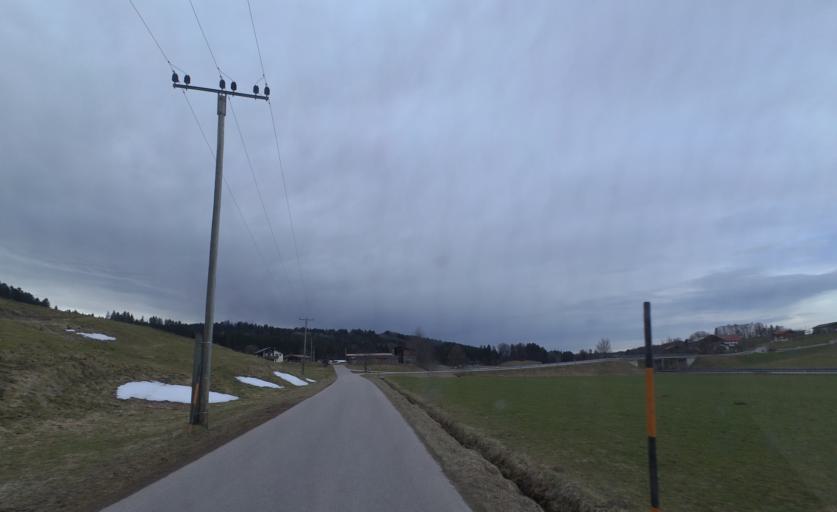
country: DE
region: Bavaria
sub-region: Upper Bavaria
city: Inzell
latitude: 47.8252
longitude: 12.7592
